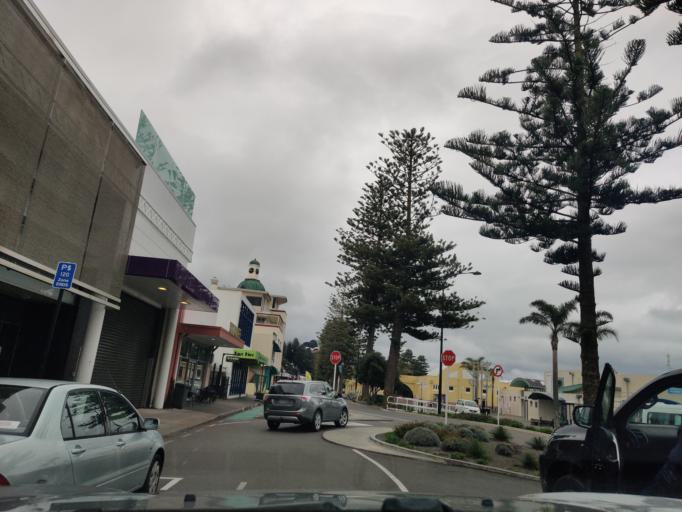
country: NZ
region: Hawke's Bay
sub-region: Napier City
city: Napier
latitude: -39.4910
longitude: 176.9192
